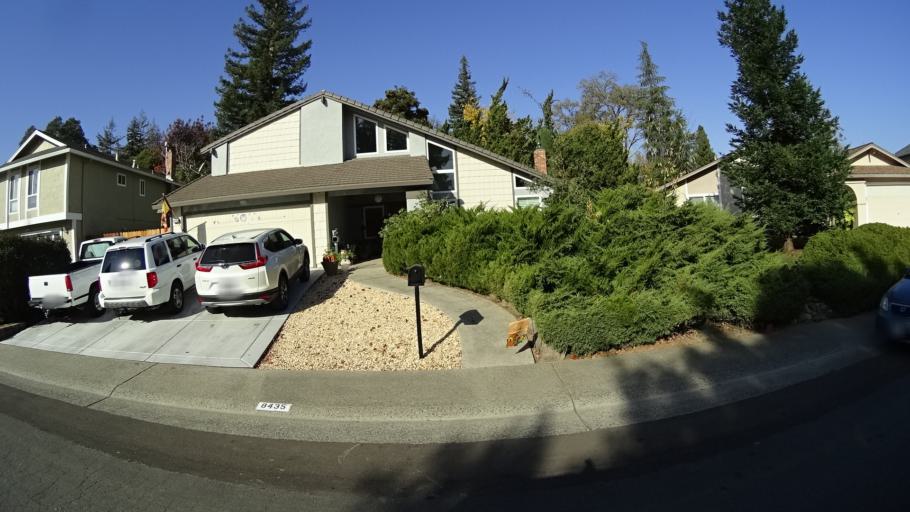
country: US
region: California
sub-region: Sacramento County
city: Orangevale
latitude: 38.6957
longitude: -121.2459
